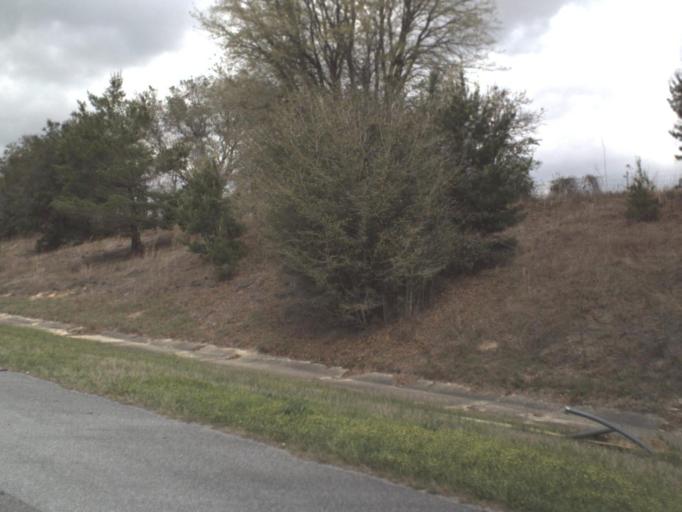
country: US
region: Florida
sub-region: Okaloosa County
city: Crestview
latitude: 30.7179
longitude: -86.4460
